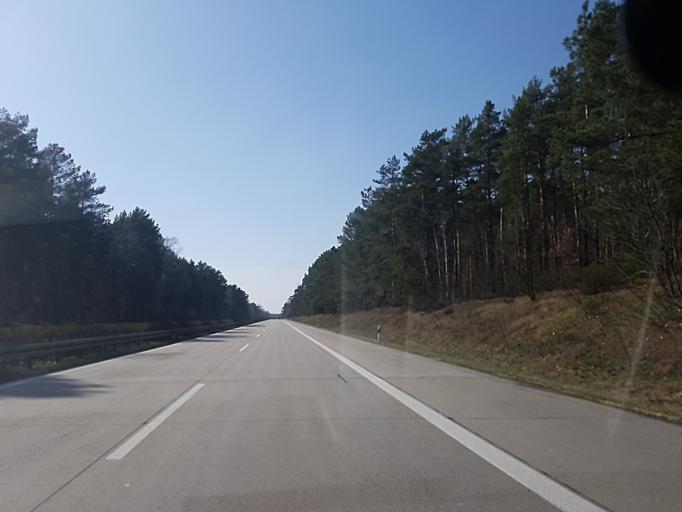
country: DE
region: Brandenburg
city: Heinersbruck
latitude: 51.7107
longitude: 14.5083
